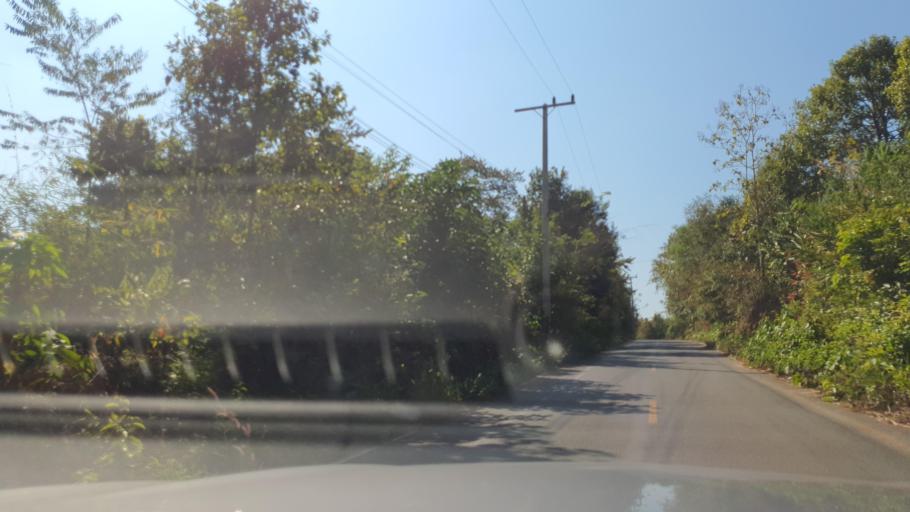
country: TH
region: Nan
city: Pua
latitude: 19.1696
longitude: 100.9095
